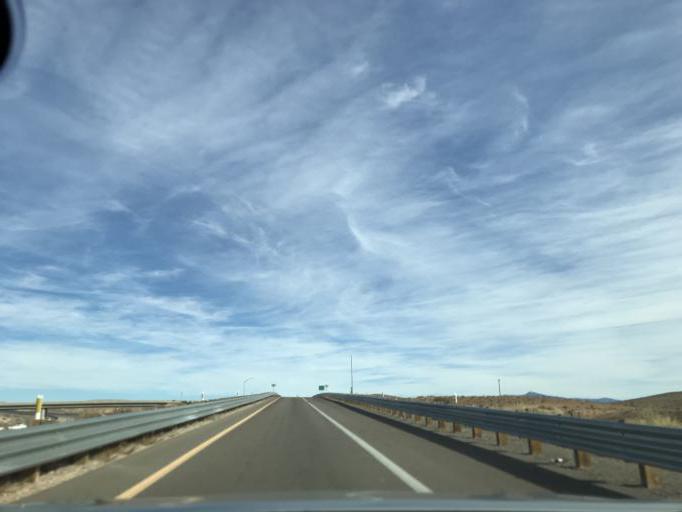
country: US
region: Nevada
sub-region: Clark County
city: Moapa Town
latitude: 36.6696
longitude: -114.5238
